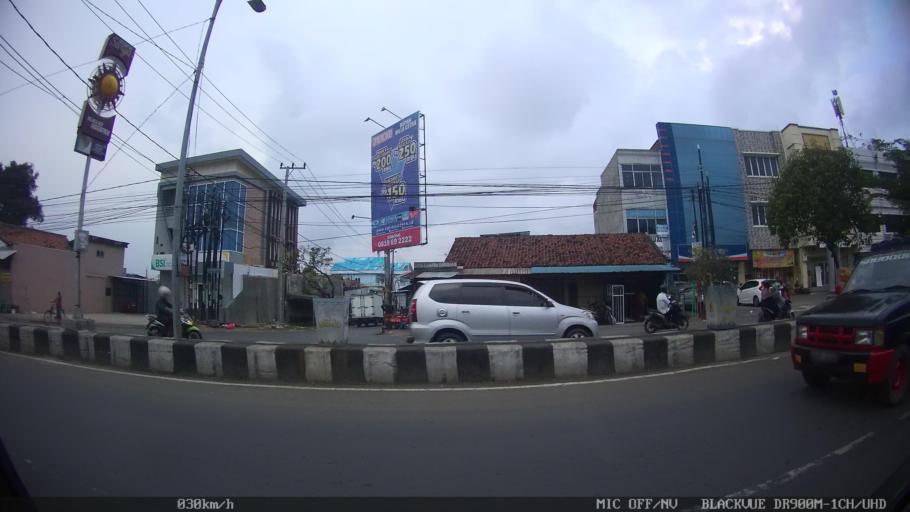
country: ID
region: Lampung
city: Bandarlampung
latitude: -5.4083
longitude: 105.2696
